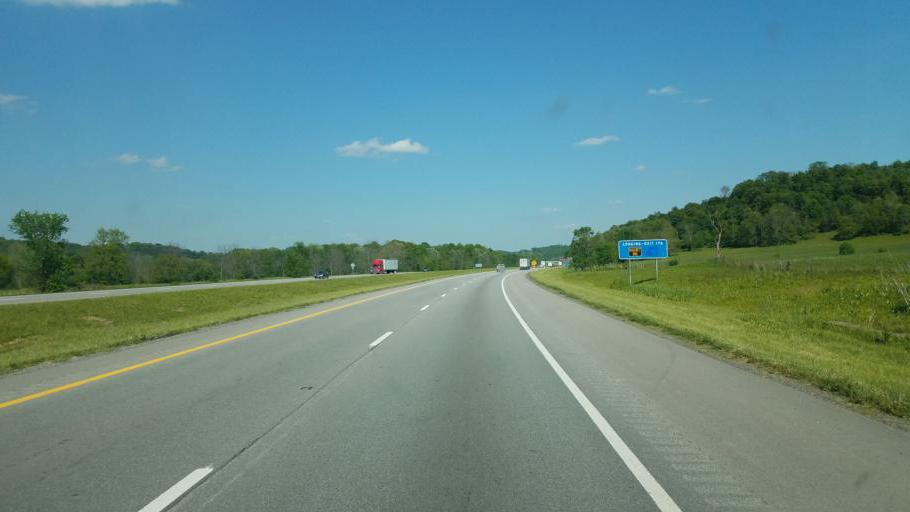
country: US
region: Ohio
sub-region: Guernsey County
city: Cambridge
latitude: 40.0078
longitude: -81.6473
